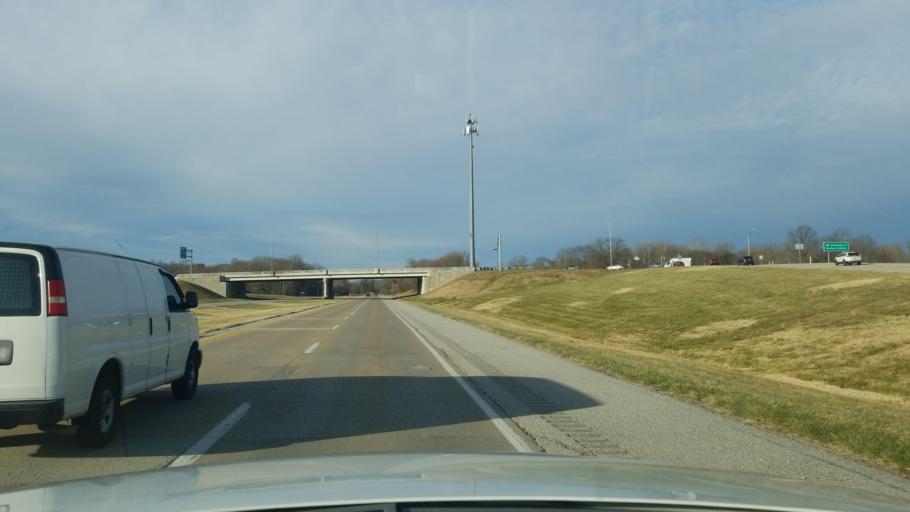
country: US
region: Indiana
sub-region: Vanderburgh County
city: Evansville
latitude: 37.9676
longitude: -87.6747
